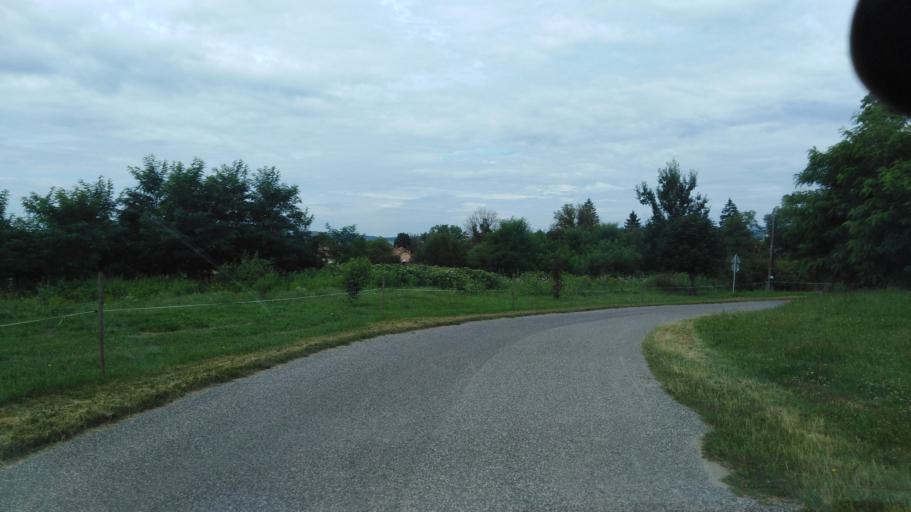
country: HU
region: Nograd
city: Karancskeszi
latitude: 48.2324
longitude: 19.6362
